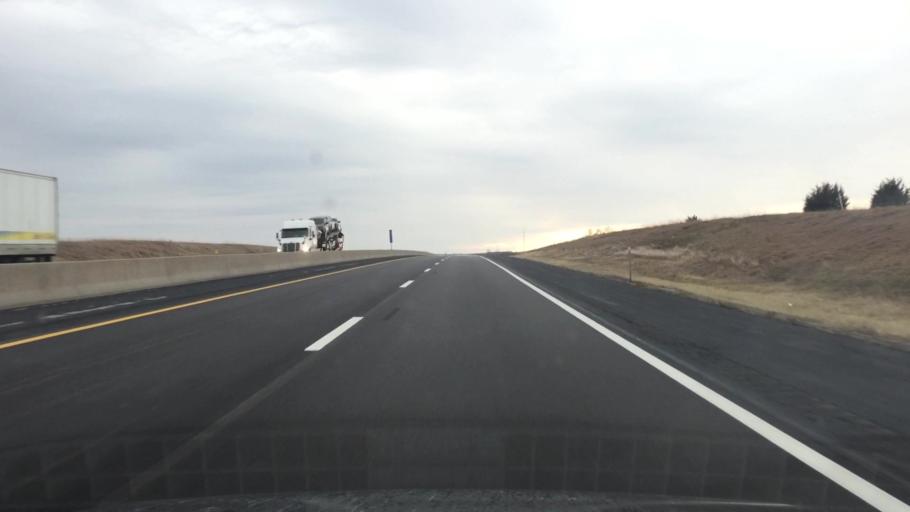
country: US
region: Kansas
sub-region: Osage County
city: Osage City
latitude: 38.7621
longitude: -95.9314
